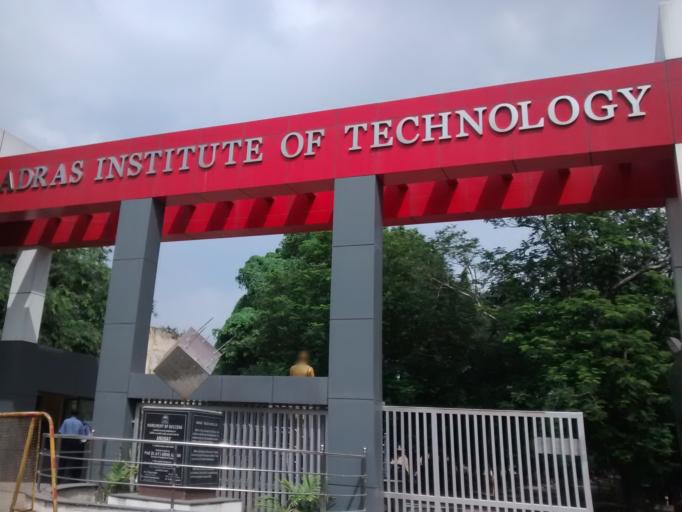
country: IN
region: Tamil Nadu
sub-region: Kancheepuram
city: Pallavaram
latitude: 12.9462
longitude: 80.1386
